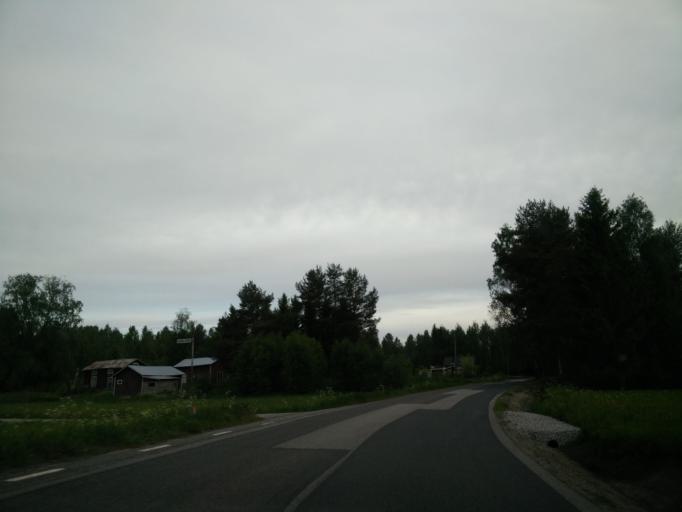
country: SE
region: Vaesternorrland
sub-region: Kramfors Kommun
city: Kramfors
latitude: 63.0376
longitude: 17.7979
